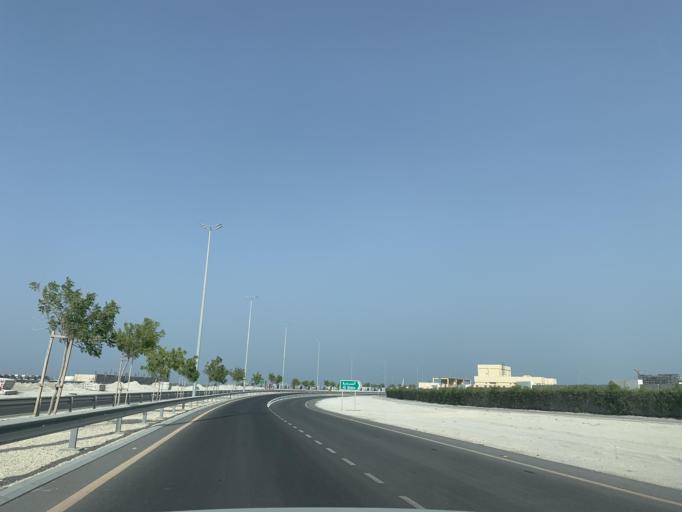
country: BH
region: Muharraq
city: Al Muharraq
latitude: 26.3118
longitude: 50.6380
